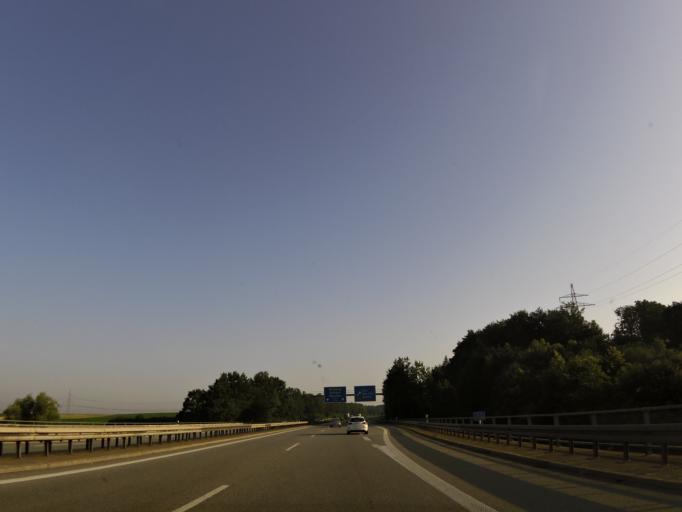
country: DE
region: Bavaria
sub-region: Swabia
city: Vohringen
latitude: 48.3172
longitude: 10.0915
